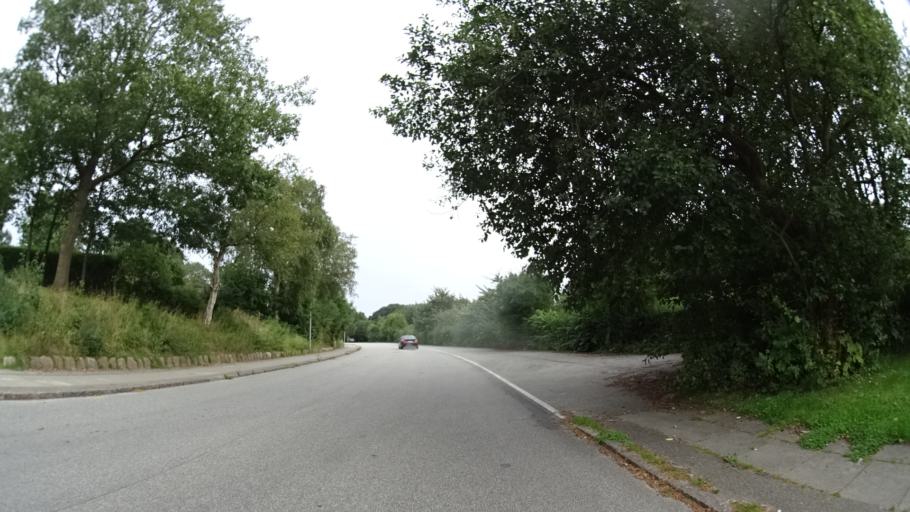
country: DK
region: Central Jutland
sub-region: Arhus Kommune
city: Stavtrup
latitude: 56.1493
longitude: 10.1293
